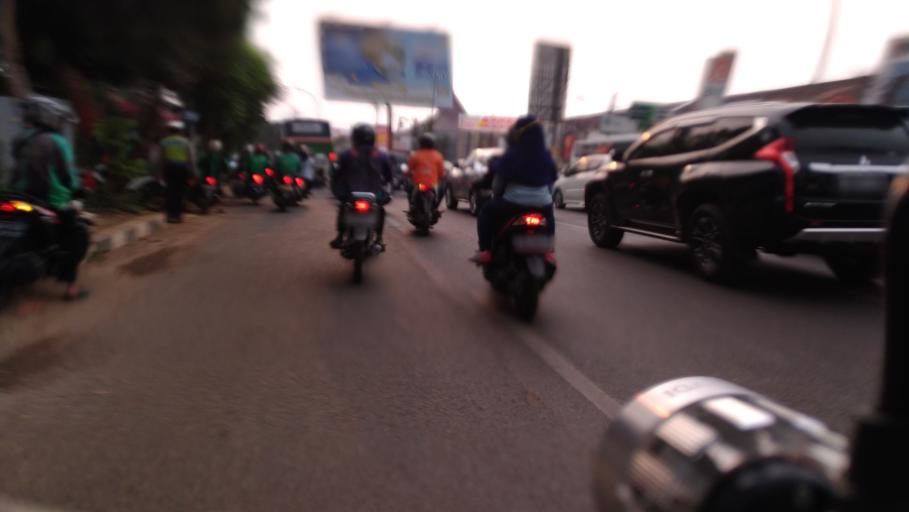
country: ID
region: West Java
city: Cileungsir
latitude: -6.3756
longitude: 106.9160
